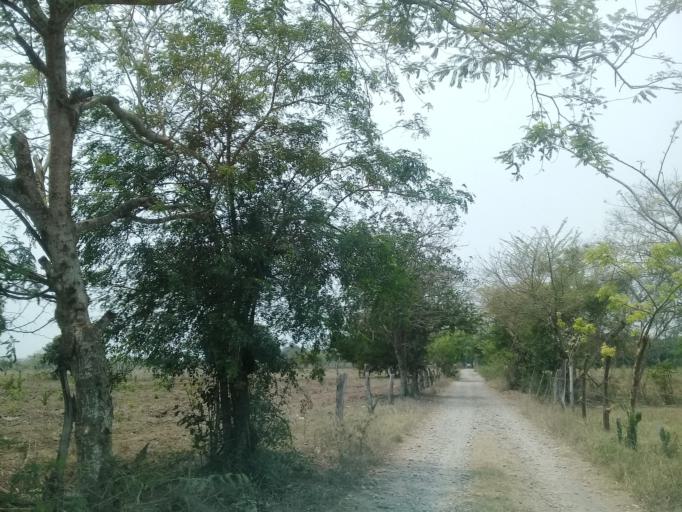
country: MX
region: Veracruz
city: Jamapa
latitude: 18.9320
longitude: -96.2049
